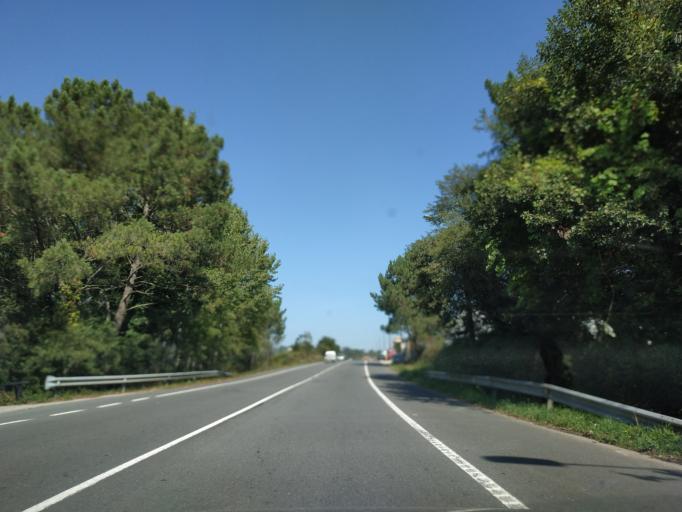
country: ES
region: Galicia
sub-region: Provincia da Coruna
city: Carballo
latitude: 43.2358
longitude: -8.6464
